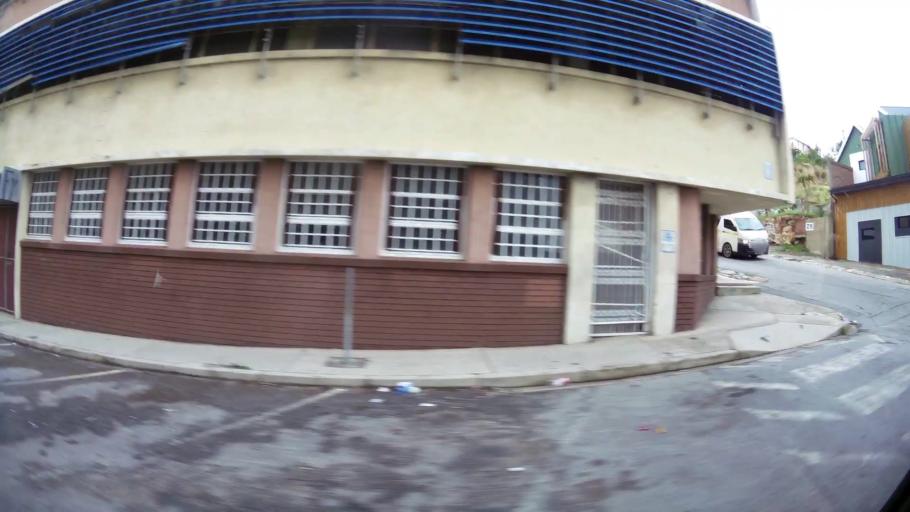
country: ZA
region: Eastern Cape
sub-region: Nelson Mandela Bay Metropolitan Municipality
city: Port Elizabeth
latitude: -33.9573
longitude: 25.6171
